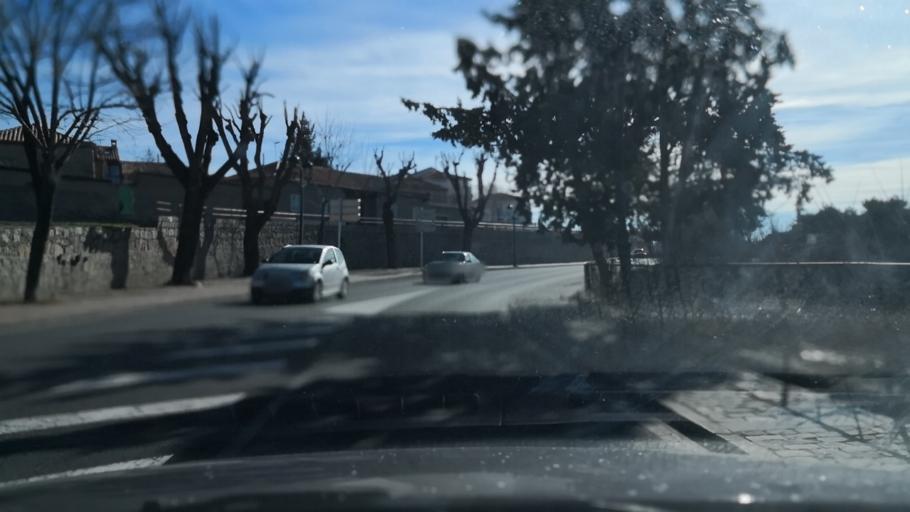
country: ES
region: Castille and Leon
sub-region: Provincia de Avila
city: Avila
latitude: 40.6551
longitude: -4.7068
